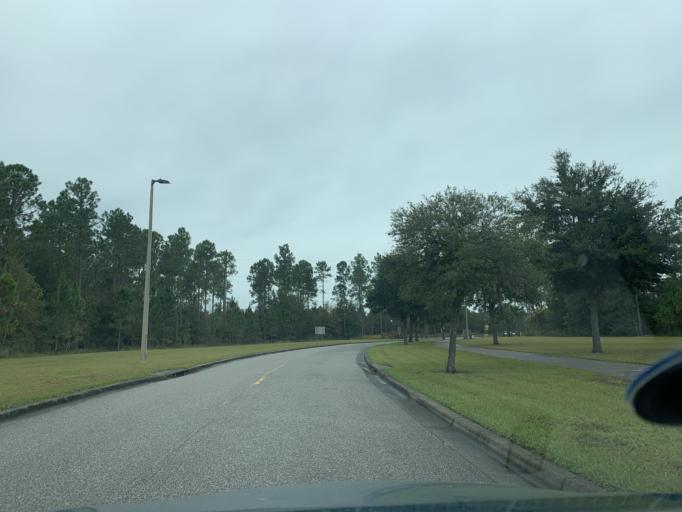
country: US
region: Florida
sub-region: Pasco County
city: Wesley Chapel
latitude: 28.2719
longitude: -82.3233
